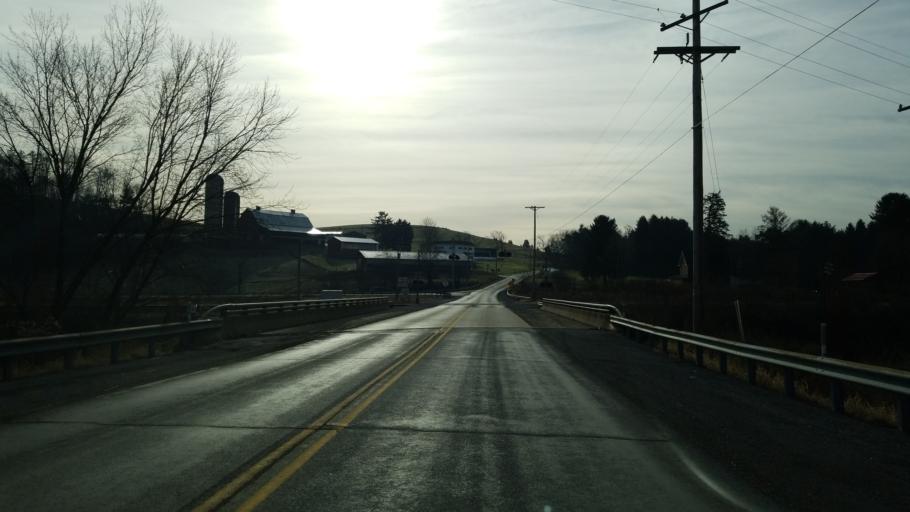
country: US
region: Pennsylvania
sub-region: Jefferson County
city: Albion
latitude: 40.9550
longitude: -78.9240
